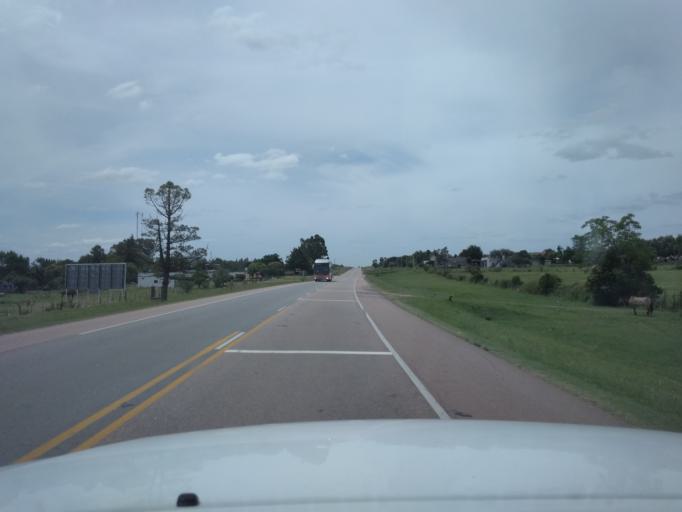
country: UY
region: Canelones
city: Canelones
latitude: -34.4974
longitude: -56.2820
